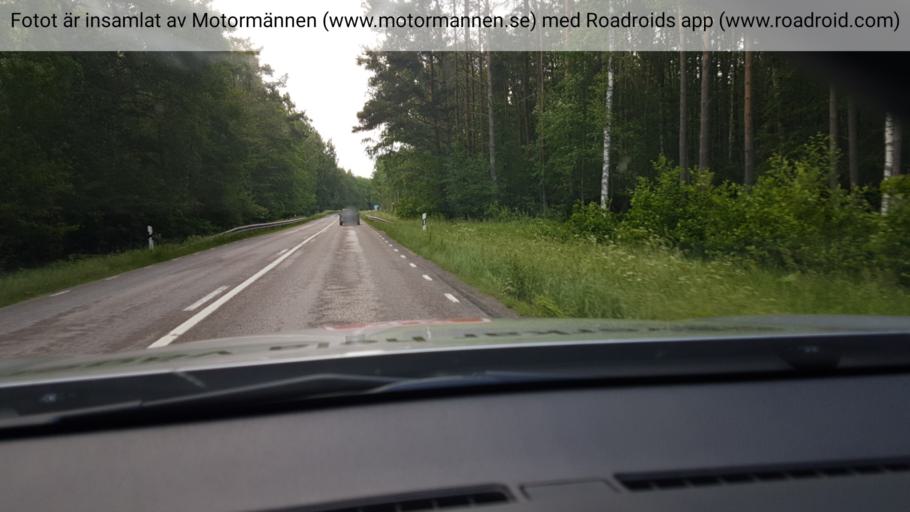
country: SE
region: Vaestra Goetaland
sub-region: Hjo Kommun
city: Hjo
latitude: 58.1804
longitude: 14.2037
